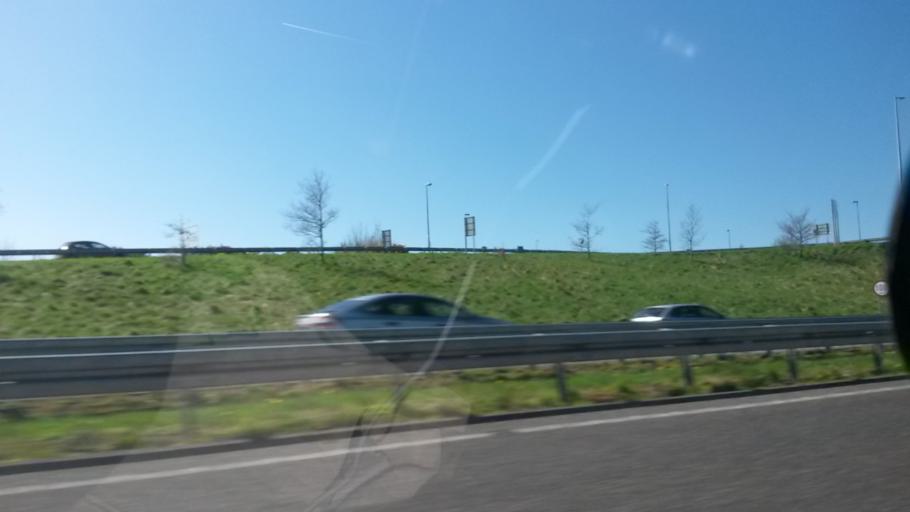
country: IE
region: Munster
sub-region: County Cork
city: Killumney
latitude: 51.8788
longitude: -8.6354
